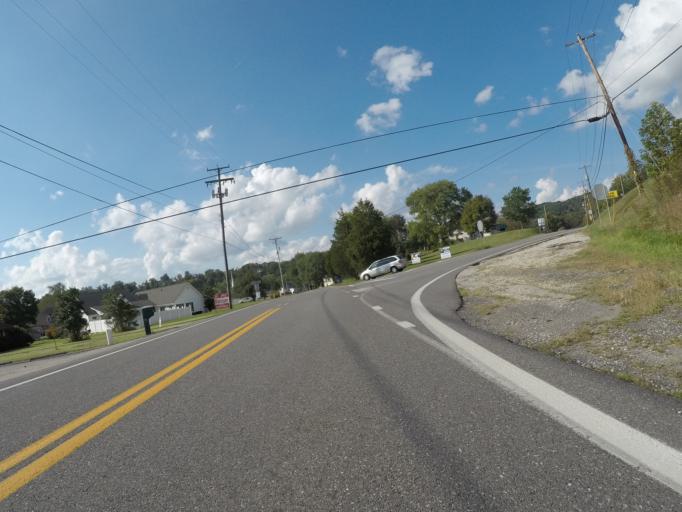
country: US
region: Ohio
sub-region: Lawrence County
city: Burlington
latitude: 38.3543
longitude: -82.5046
